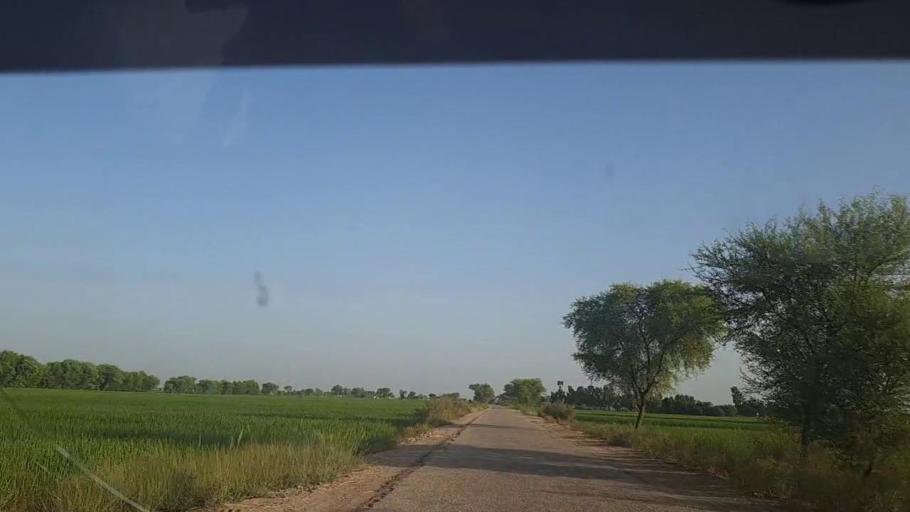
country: PK
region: Sindh
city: Thul
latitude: 28.2086
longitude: 68.8706
